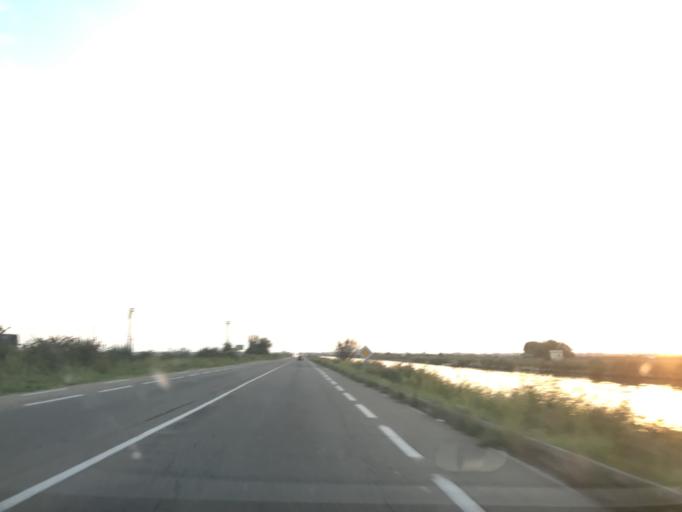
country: FR
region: Languedoc-Roussillon
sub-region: Departement du Gard
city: Aigues-Mortes
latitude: 43.5504
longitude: 4.1671
